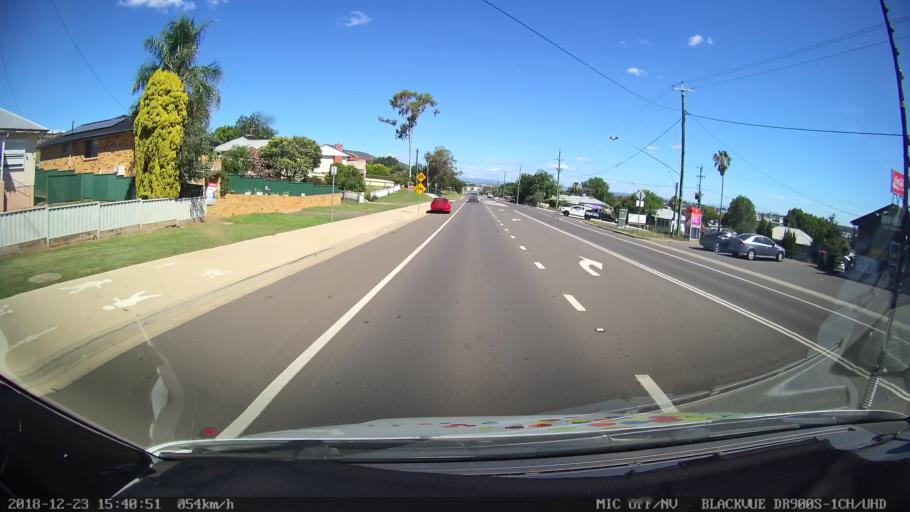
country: AU
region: New South Wales
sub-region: Tamworth Municipality
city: Tamworth
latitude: -31.0732
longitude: 150.9127
